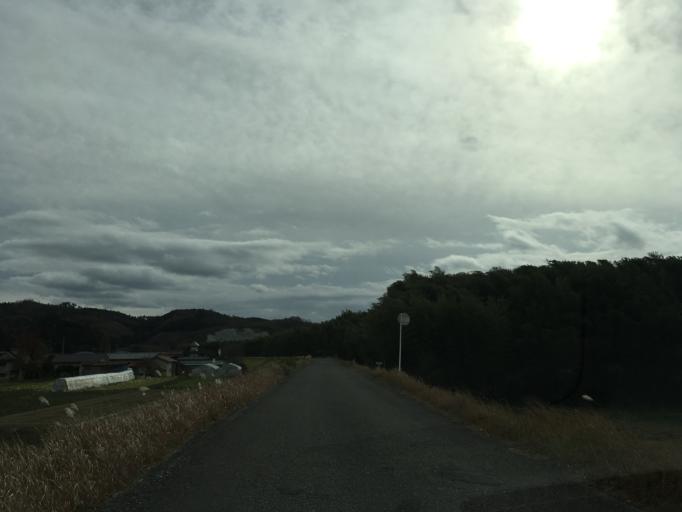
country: JP
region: Iwate
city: Ichinoseki
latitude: 38.7581
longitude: 141.2779
